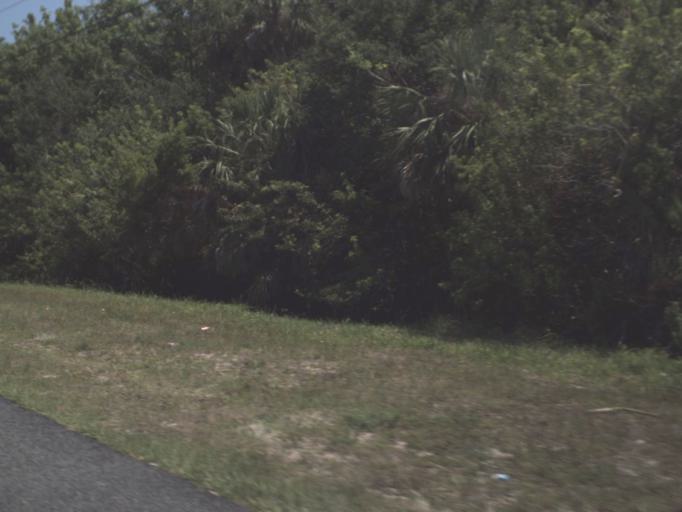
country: US
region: Florida
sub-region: Brevard County
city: Grant-Valkaria
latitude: 27.9667
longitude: -80.5434
